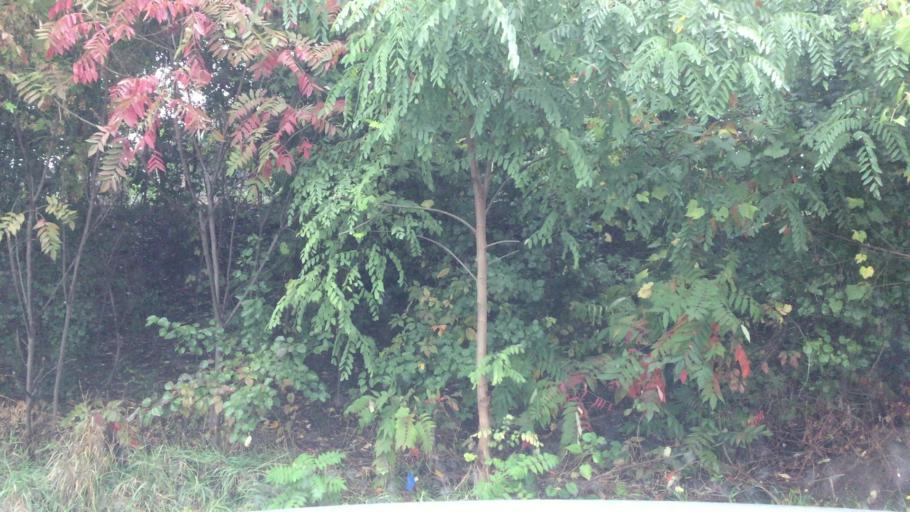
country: US
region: Michigan
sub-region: Kalamazoo County
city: Portage
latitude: 42.2203
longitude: -85.5906
